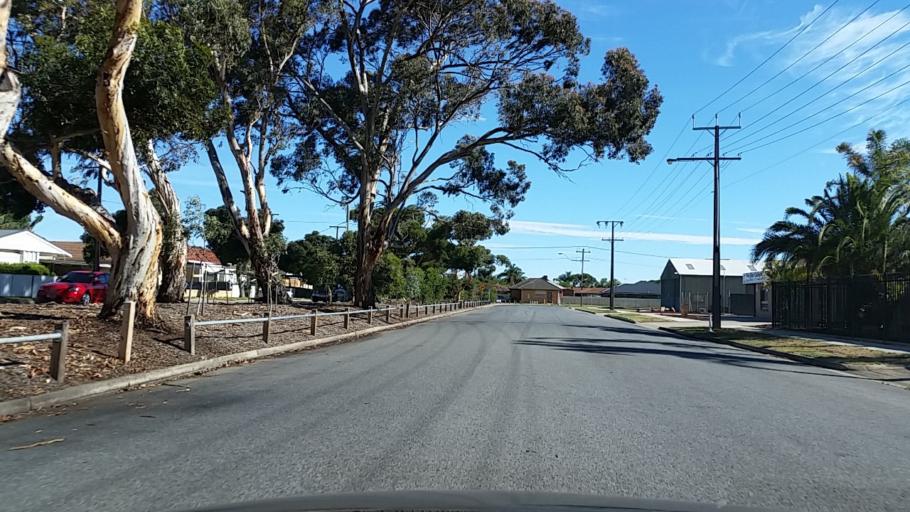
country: AU
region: South Australia
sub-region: Charles Sturt
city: Royal Park
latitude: -34.8671
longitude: 138.5074
